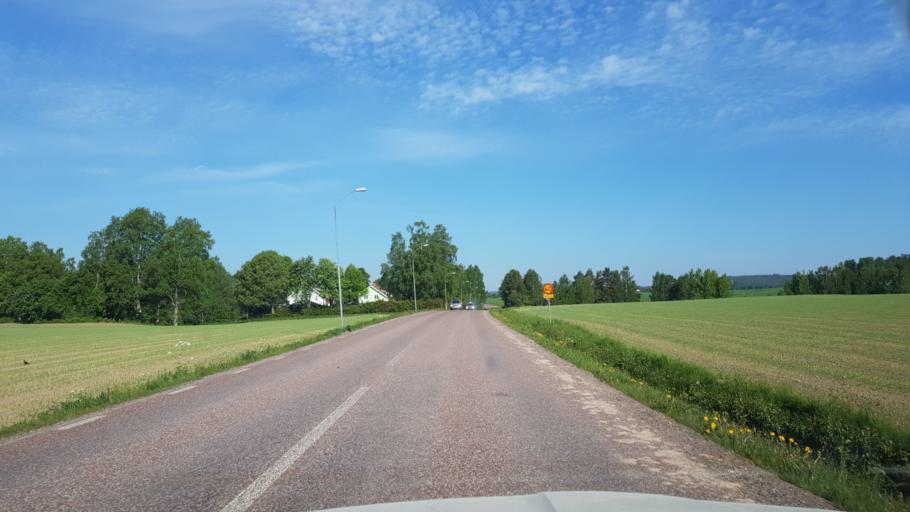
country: SE
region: Dalarna
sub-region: Saters Kommun
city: Saeter
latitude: 60.4131
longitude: 15.7904
